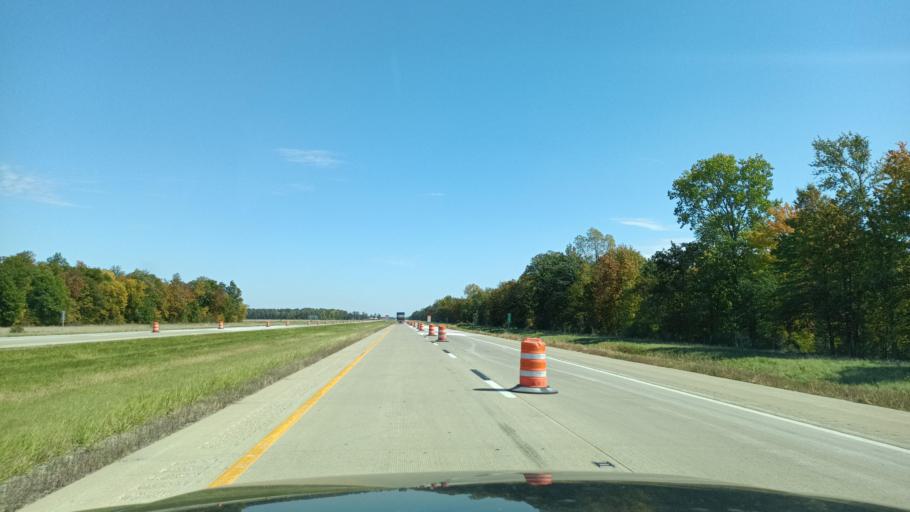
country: US
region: Ohio
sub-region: Paulding County
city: Paulding
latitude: 41.2425
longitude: -84.5099
